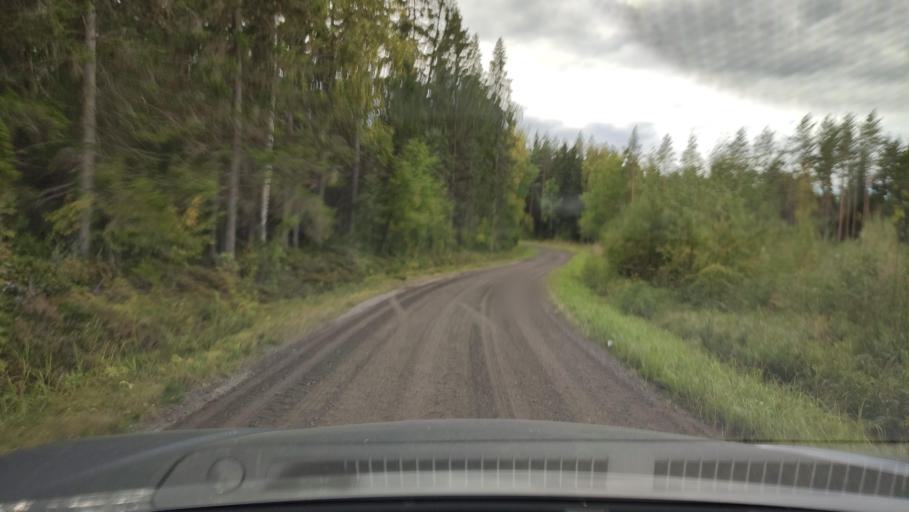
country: FI
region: Southern Ostrobothnia
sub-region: Suupohja
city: Karijoki
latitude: 62.2171
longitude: 21.5702
